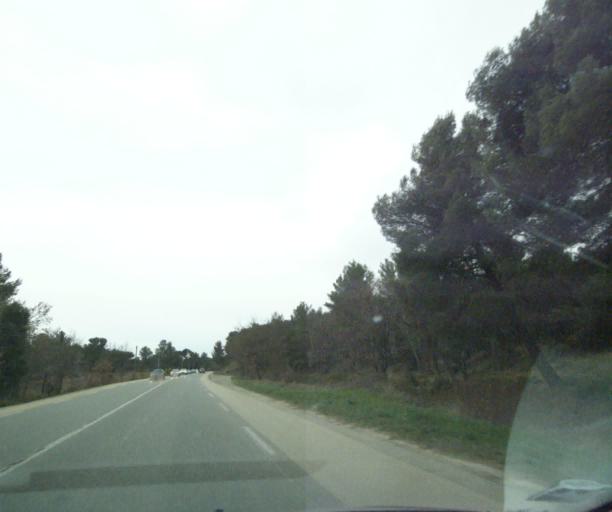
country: FR
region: Provence-Alpes-Cote d'Azur
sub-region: Departement des Bouches-du-Rhone
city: Meyrargues
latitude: 43.6273
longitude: 5.5098
